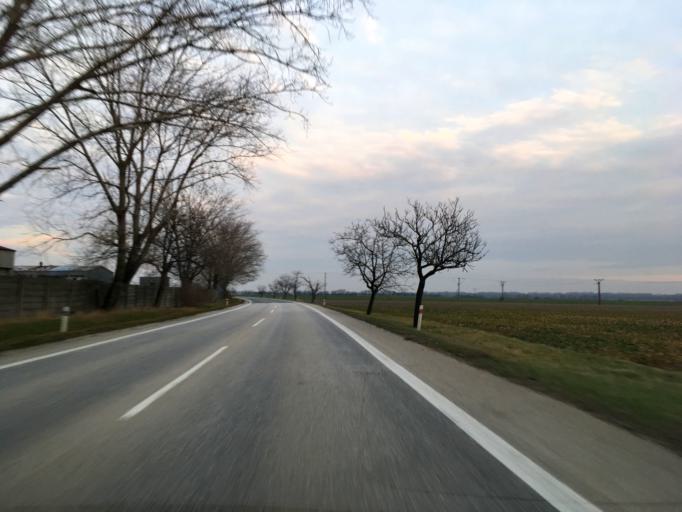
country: HU
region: Komarom-Esztergom
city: Acs
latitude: 47.7644
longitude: 17.9825
